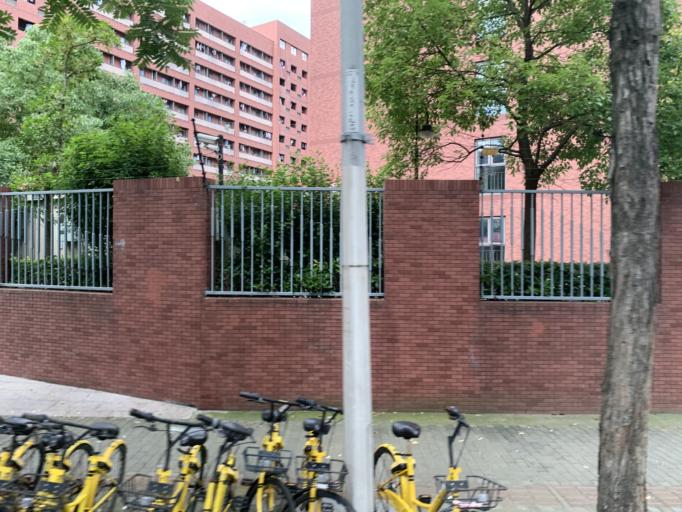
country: CN
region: Shanghai Shi
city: Huamu
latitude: 31.2037
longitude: 121.5290
